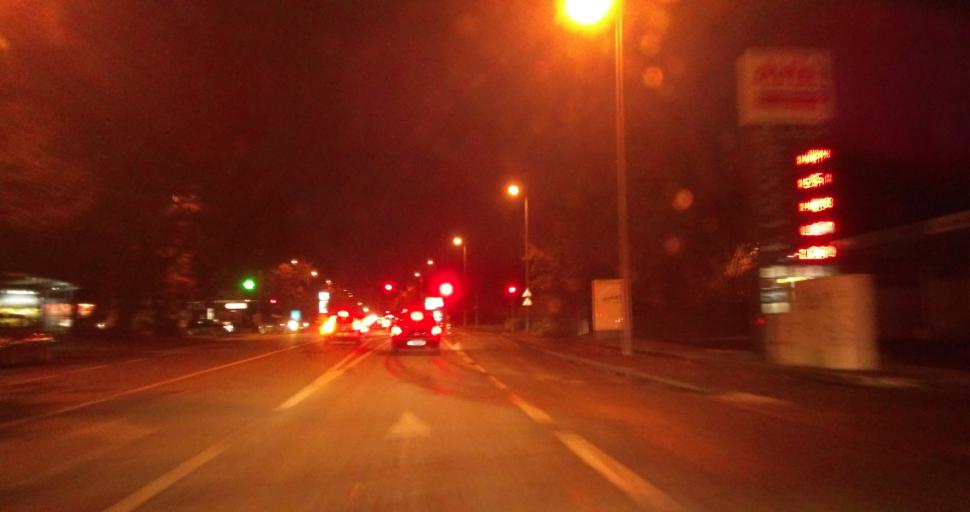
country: FR
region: Brittany
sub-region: Departement d'Ille-et-Vilaine
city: Chantepie
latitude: 48.0978
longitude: -1.6430
